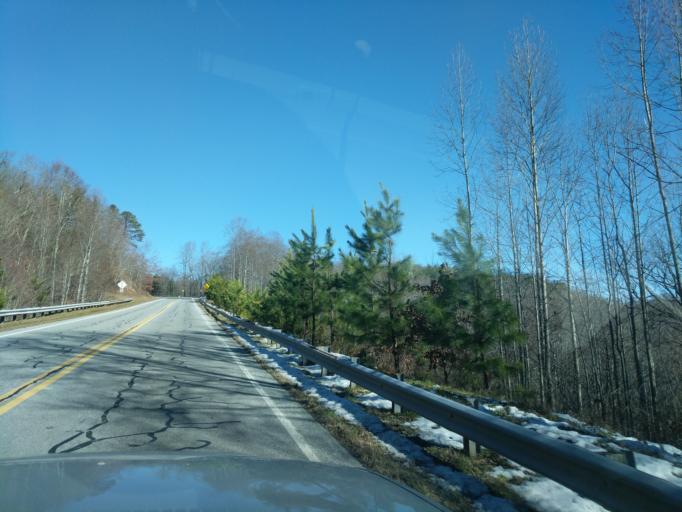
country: US
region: Georgia
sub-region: Rabun County
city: Clayton
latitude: 34.8793
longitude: -83.5781
